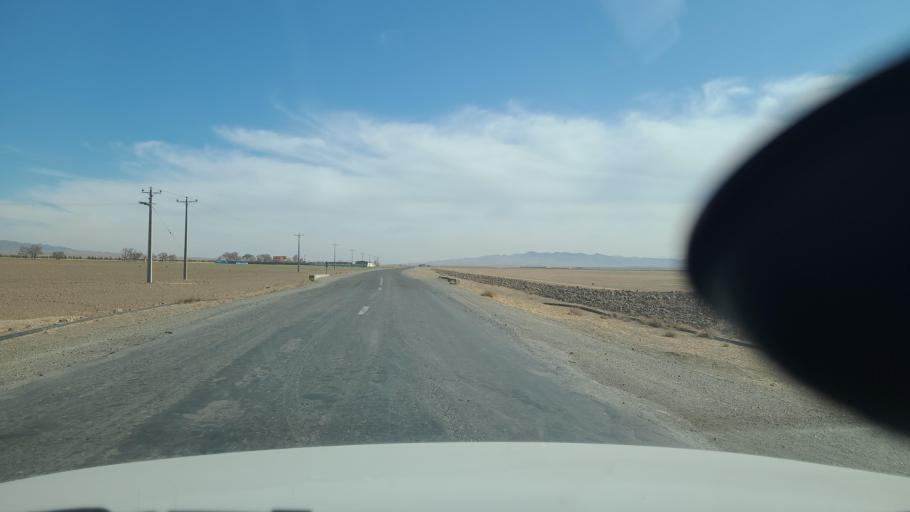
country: IR
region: Razavi Khorasan
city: Dowlatabad
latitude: 35.6000
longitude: 59.4642
